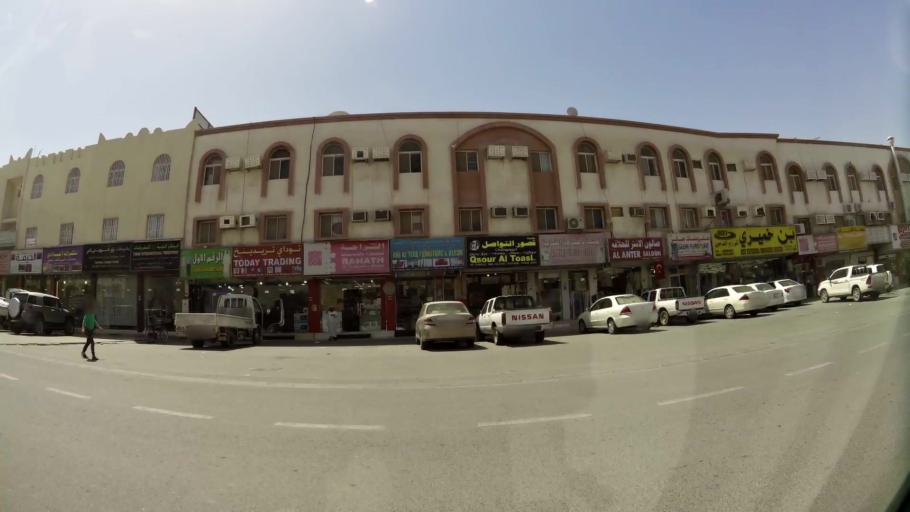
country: QA
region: Baladiyat ar Rayyan
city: Ar Rayyan
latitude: 25.2727
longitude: 51.4076
